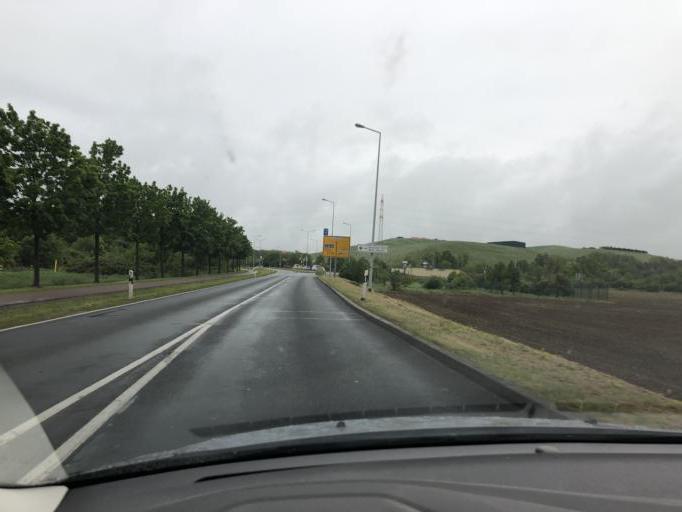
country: DE
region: Saxony-Anhalt
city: Dessau
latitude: 51.8124
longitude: 12.2156
